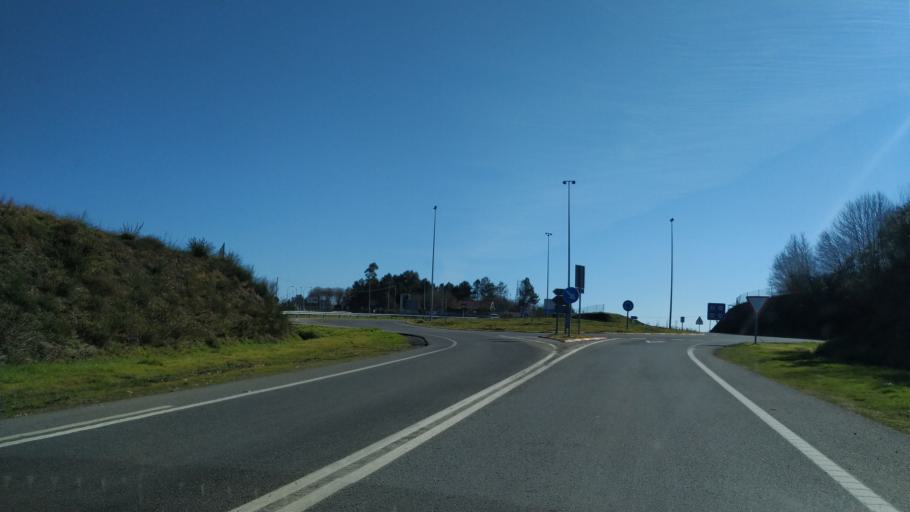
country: ES
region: Galicia
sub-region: Provincia de Pontevedra
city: Lalin
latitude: 42.6740
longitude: -8.1624
